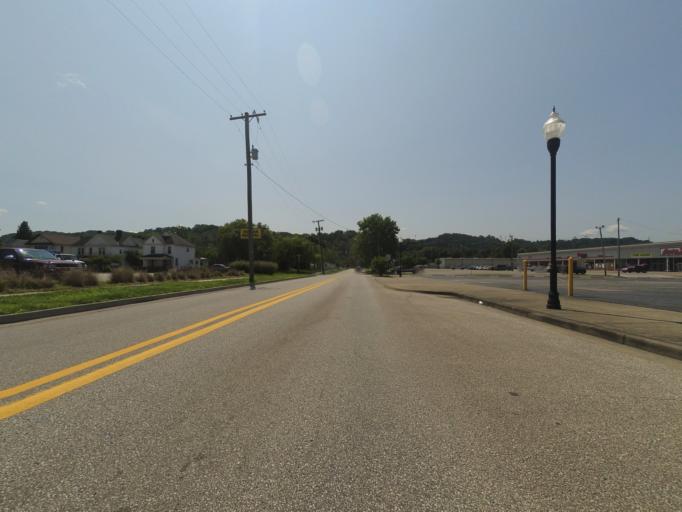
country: US
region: West Virginia
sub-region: Cabell County
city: Huntington
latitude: 38.4087
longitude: -82.4785
